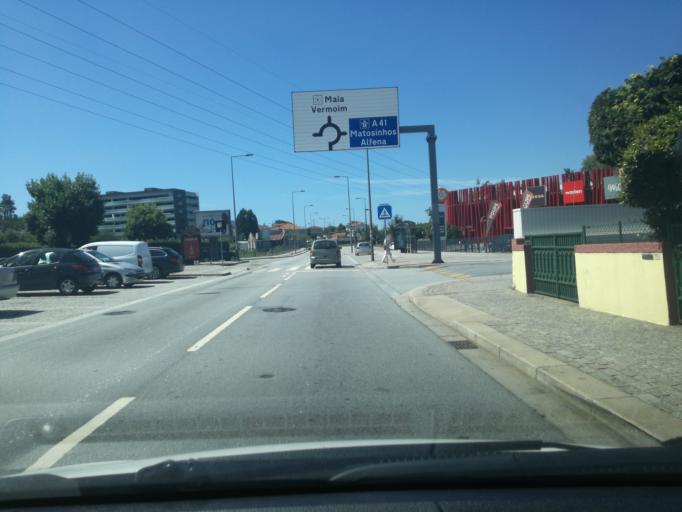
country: PT
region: Porto
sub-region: Maia
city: Nogueira
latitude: 41.2354
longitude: -8.5971
